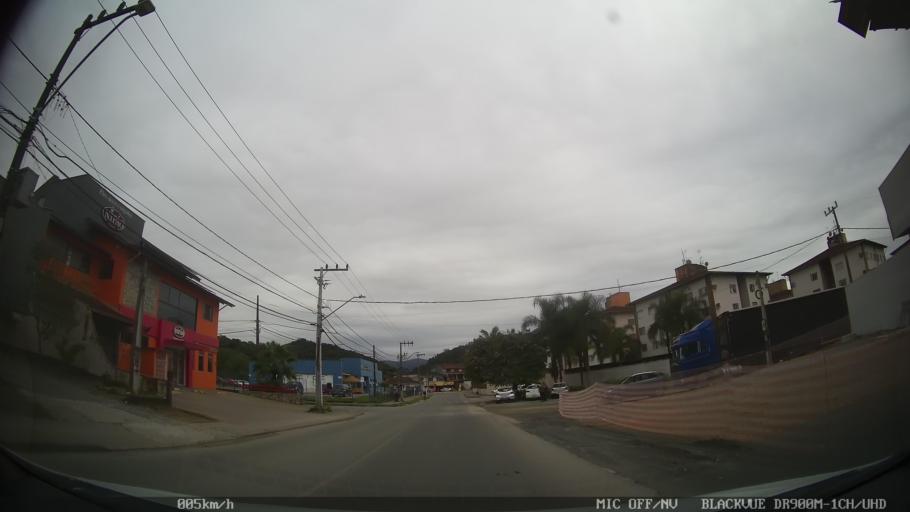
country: BR
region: Santa Catarina
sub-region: Joinville
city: Joinville
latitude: -26.2694
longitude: -48.8898
